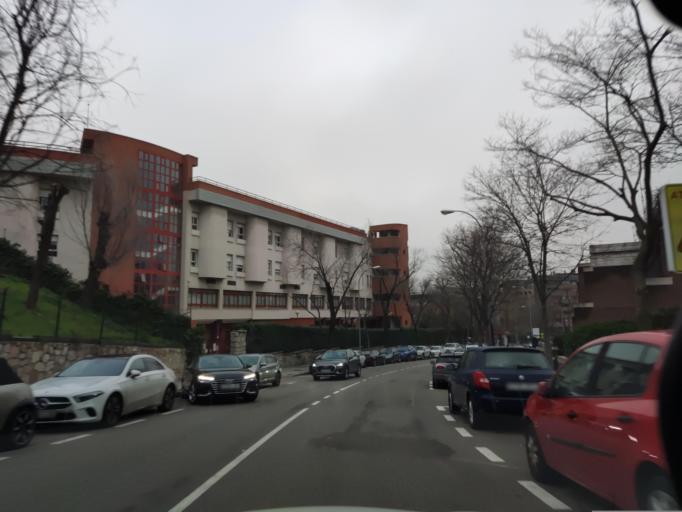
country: ES
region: Madrid
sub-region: Provincia de Madrid
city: Fuencarral-El Pardo
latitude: 40.4901
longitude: -3.7143
